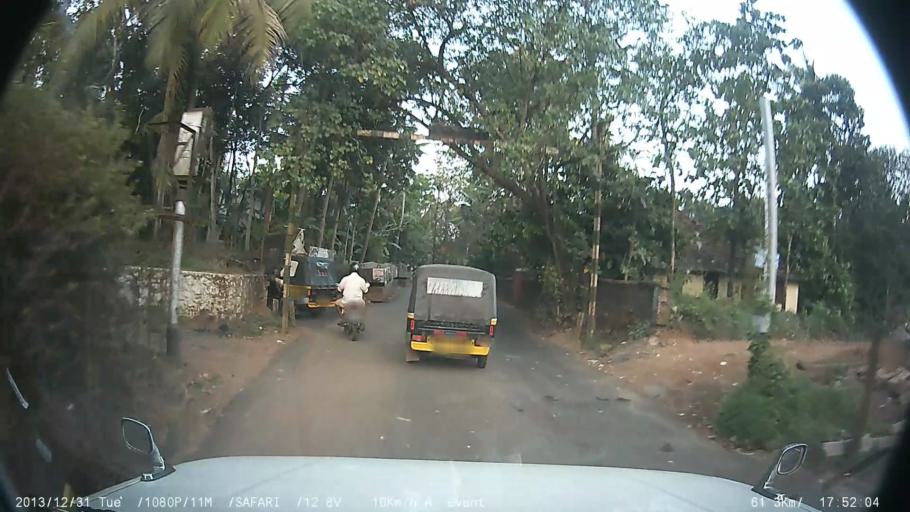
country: IN
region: Kerala
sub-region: Kottayam
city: Vaikam
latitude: 9.7561
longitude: 76.4923
